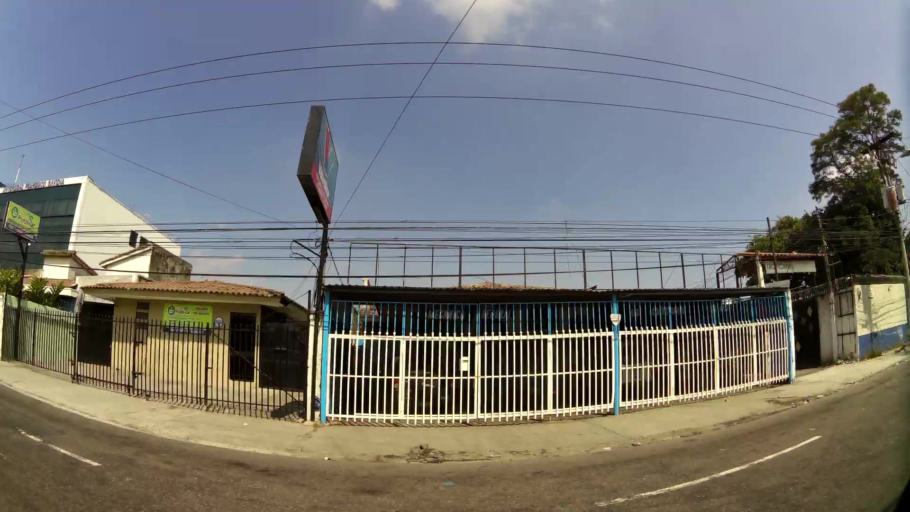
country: SV
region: San Salvador
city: San Salvador
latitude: 13.6965
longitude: -89.2188
